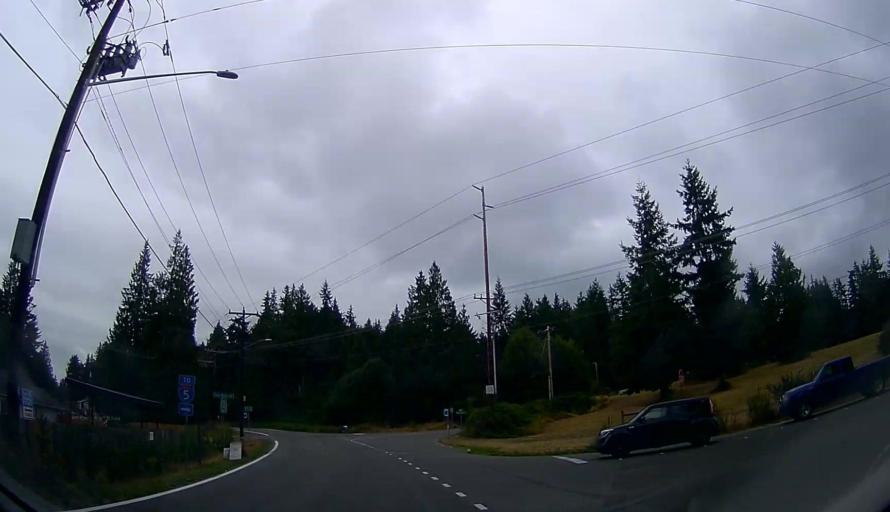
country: US
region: Washington
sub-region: Snohomish County
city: Warm Beach
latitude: 48.1882
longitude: -122.3404
